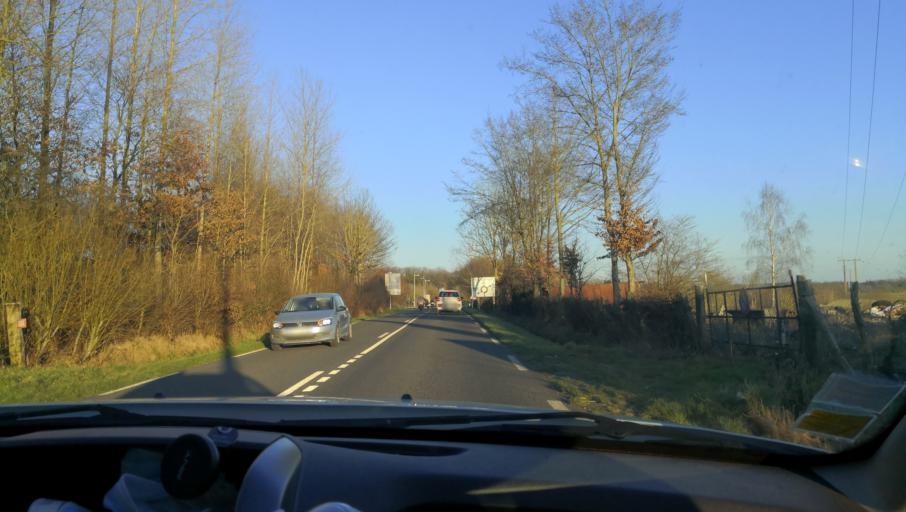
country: FR
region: Haute-Normandie
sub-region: Departement de la Seine-Maritime
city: Forges-les-Eaux
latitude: 49.6086
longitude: 1.5083
